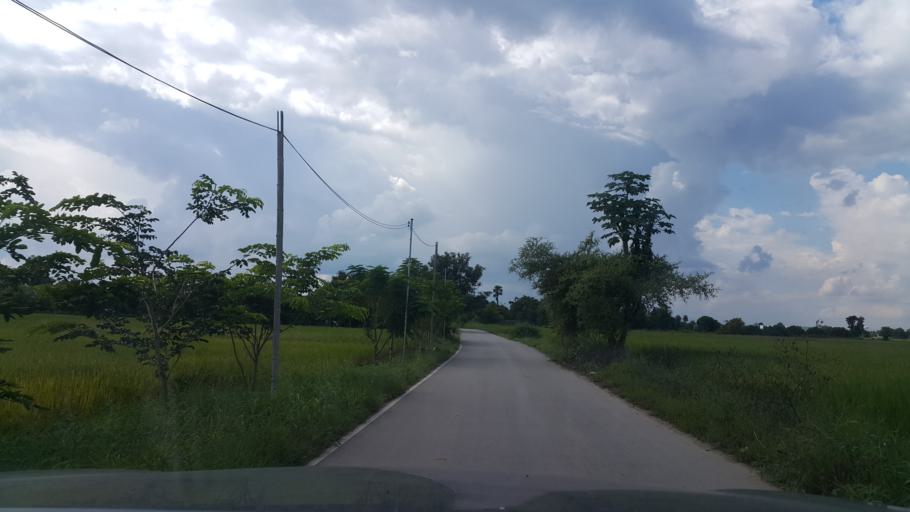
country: TH
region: Chiang Mai
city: San Kamphaeng
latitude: 18.7102
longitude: 99.1571
